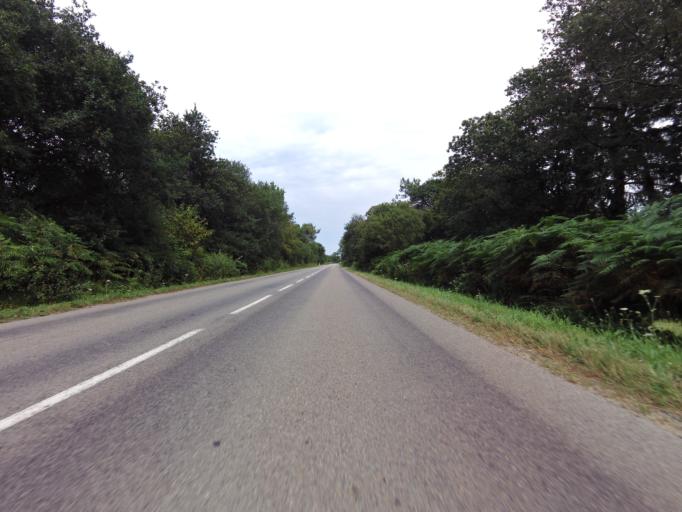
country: FR
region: Brittany
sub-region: Departement du Finistere
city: Poullan-sur-Mer
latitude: 48.0764
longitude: -4.4475
